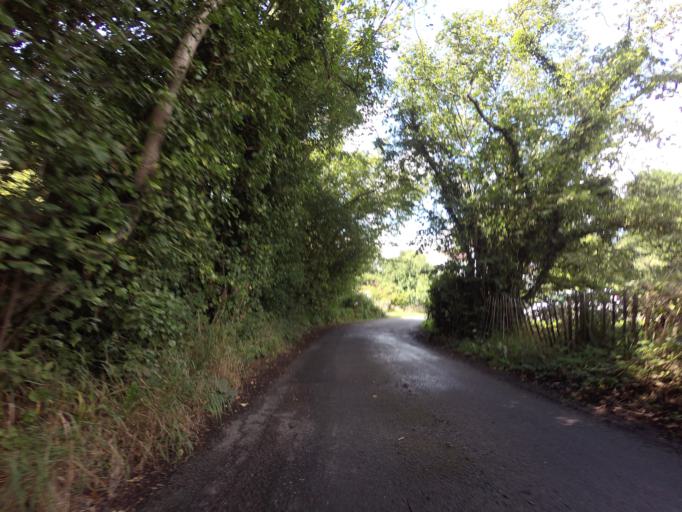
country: GB
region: England
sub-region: Kent
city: Borough Green
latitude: 51.2685
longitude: 0.2924
